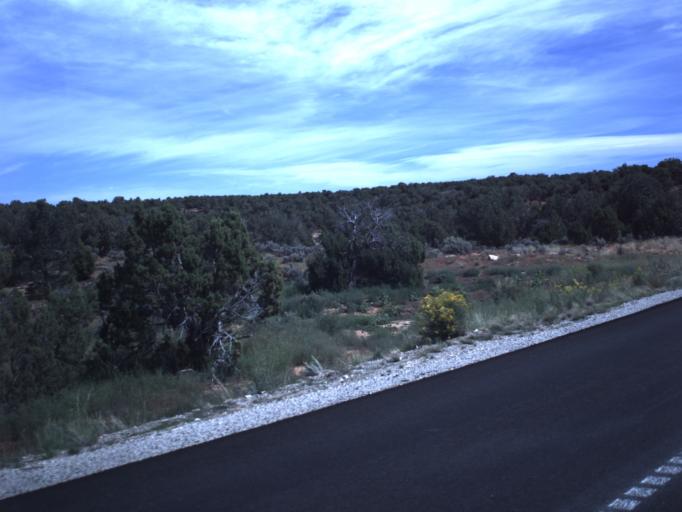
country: US
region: Utah
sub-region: San Juan County
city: Blanding
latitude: 37.5767
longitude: -109.5238
